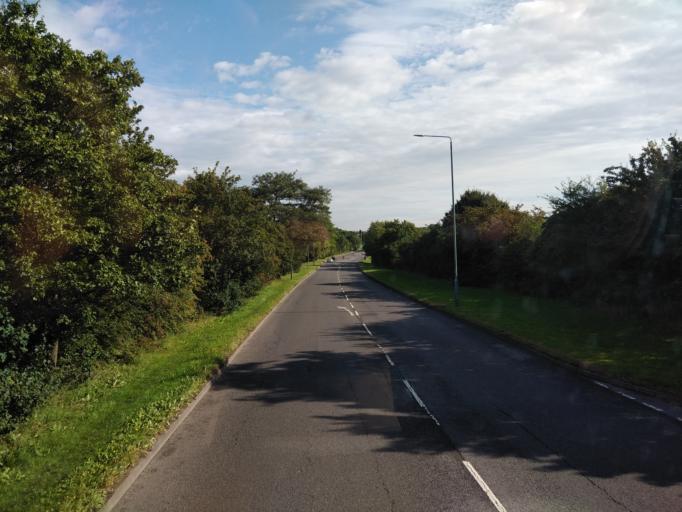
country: GB
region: England
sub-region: Nottinghamshire
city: Kimberley
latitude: 52.9577
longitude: -1.2447
